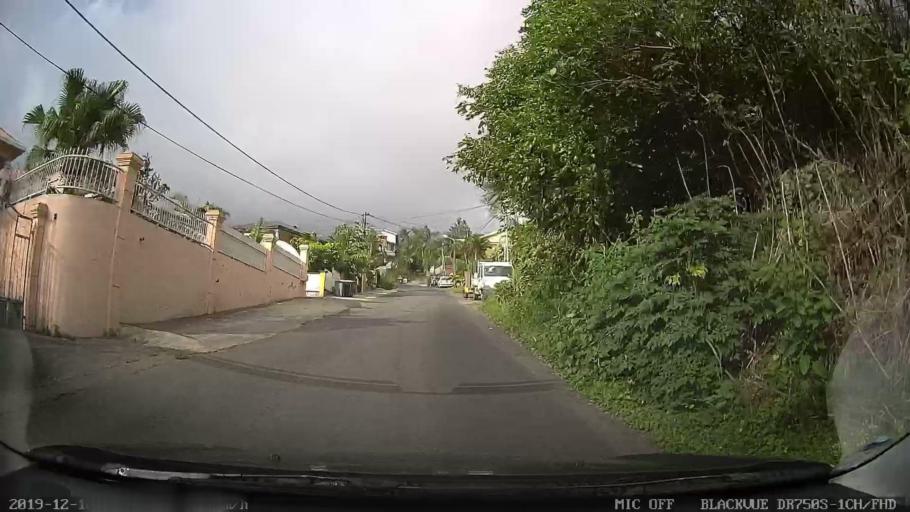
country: RE
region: Reunion
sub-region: Reunion
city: Le Tampon
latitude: -21.2564
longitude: 55.5162
